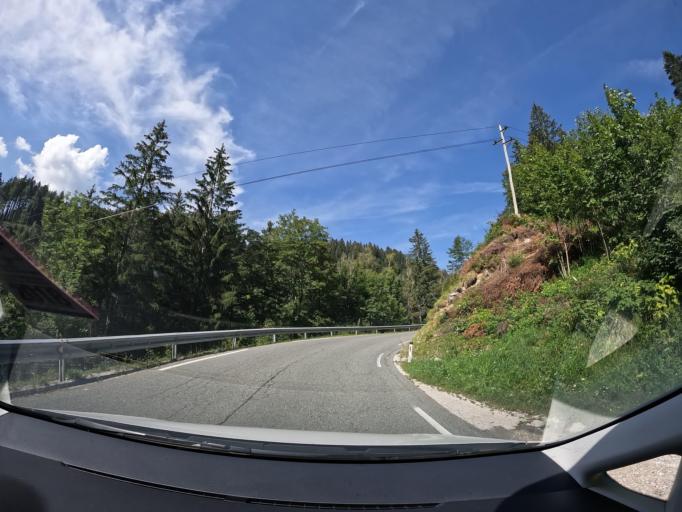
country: AT
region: Carinthia
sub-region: Politischer Bezirk Villach Land
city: Sankt Jakob
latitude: 46.5554
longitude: 14.0784
